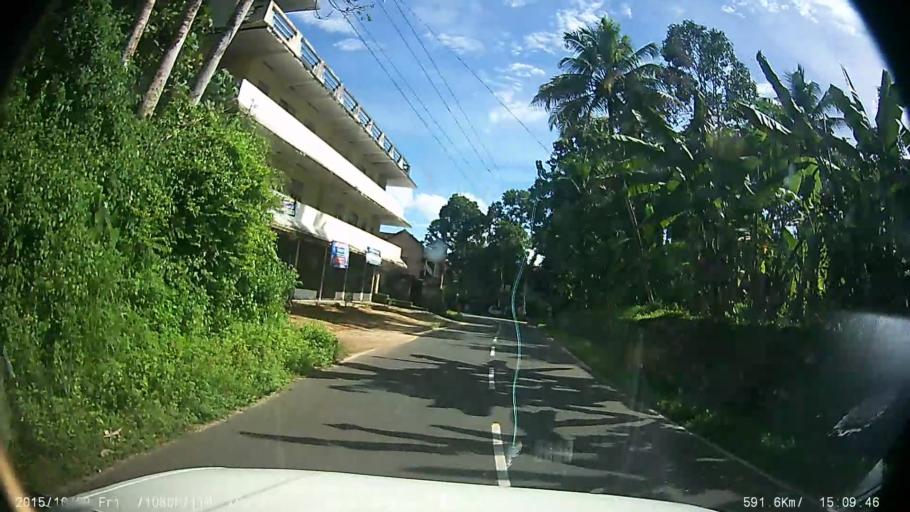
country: IN
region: Kerala
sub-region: Ernakulam
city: Piravam
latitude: 9.8839
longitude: 76.5734
